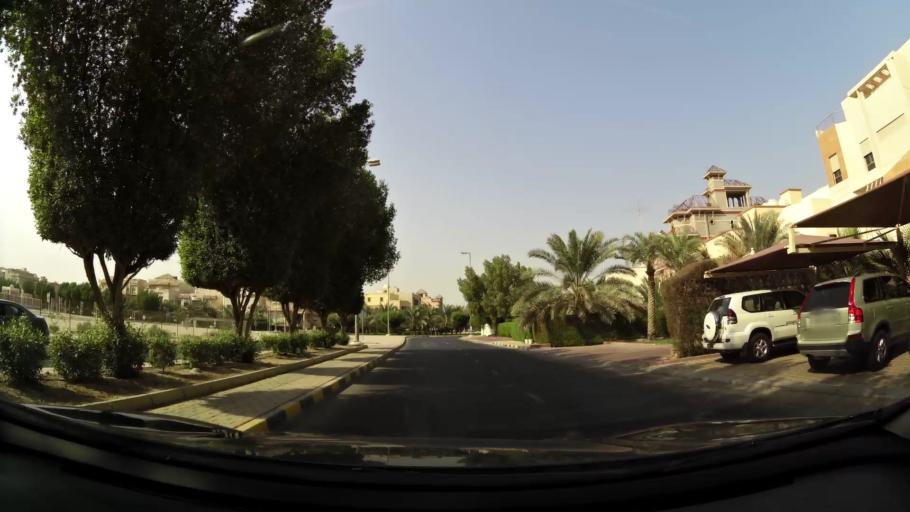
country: KW
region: Mubarak al Kabir
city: Sabah as Salim
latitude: 29.2778
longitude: 48.0475
